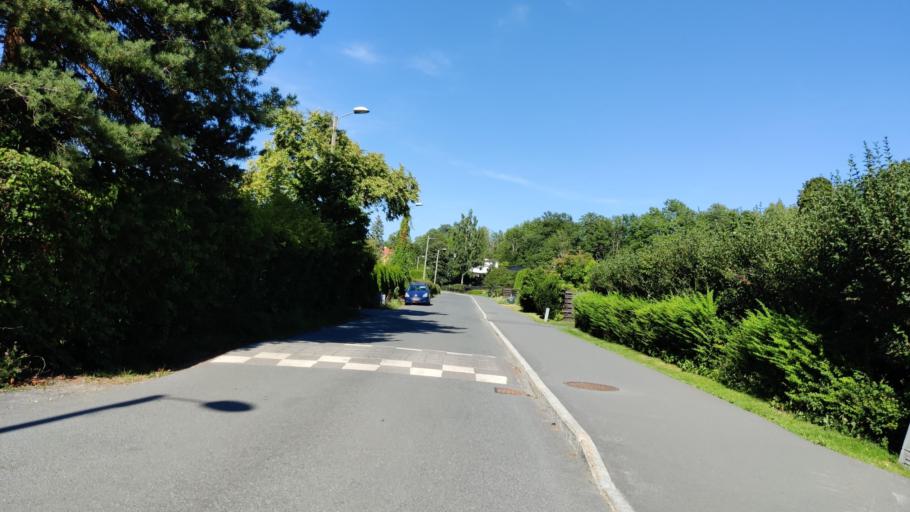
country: NO
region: Akershus
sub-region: Baerum
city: Lysaker
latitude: 59.9284
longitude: 10.6011
